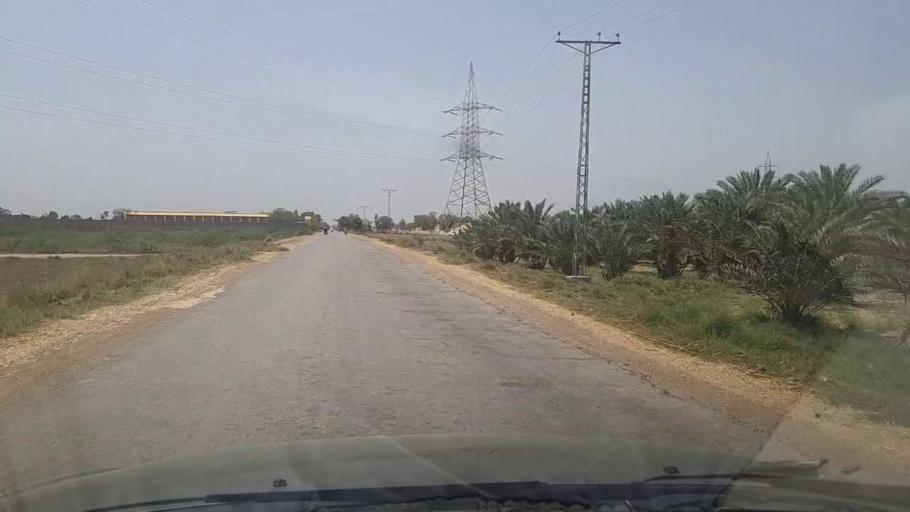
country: PK
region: Sindh
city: Karaundi
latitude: 26.8792
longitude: 68.3144
